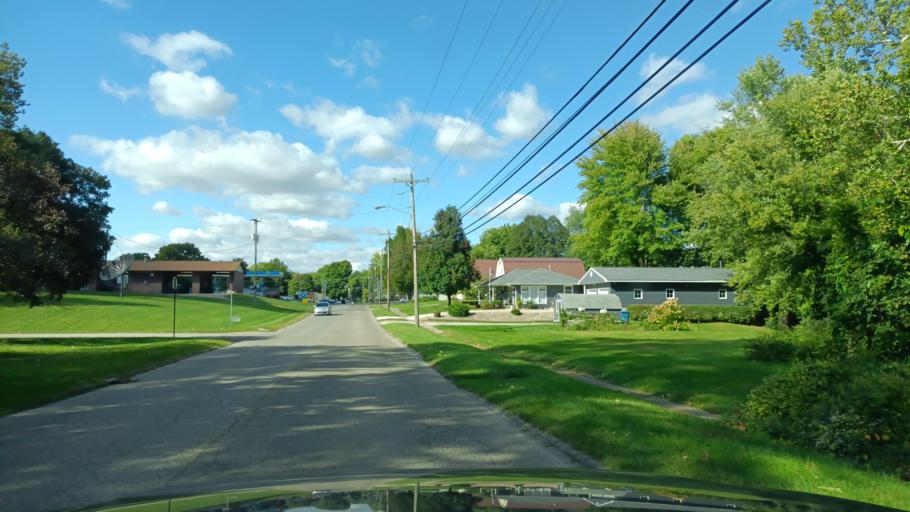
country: US
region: Indiana
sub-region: Fountain County
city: Covington
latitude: 40.1359
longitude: -87.3864
